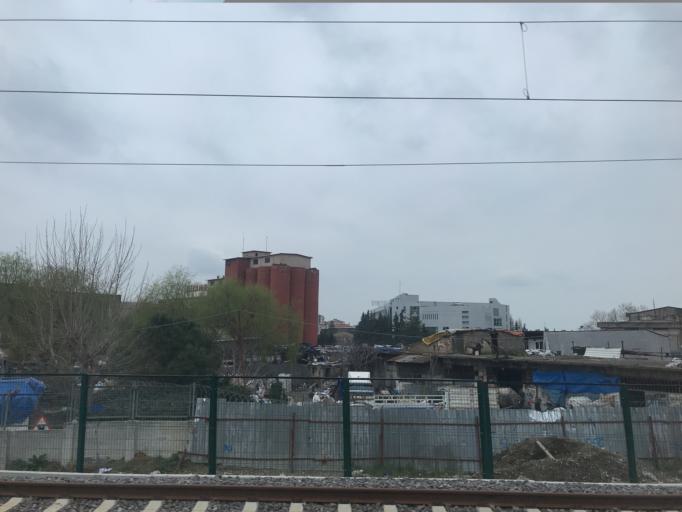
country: TR
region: Istanbul
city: Maltepe
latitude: 40.9172
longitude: 29.1416
